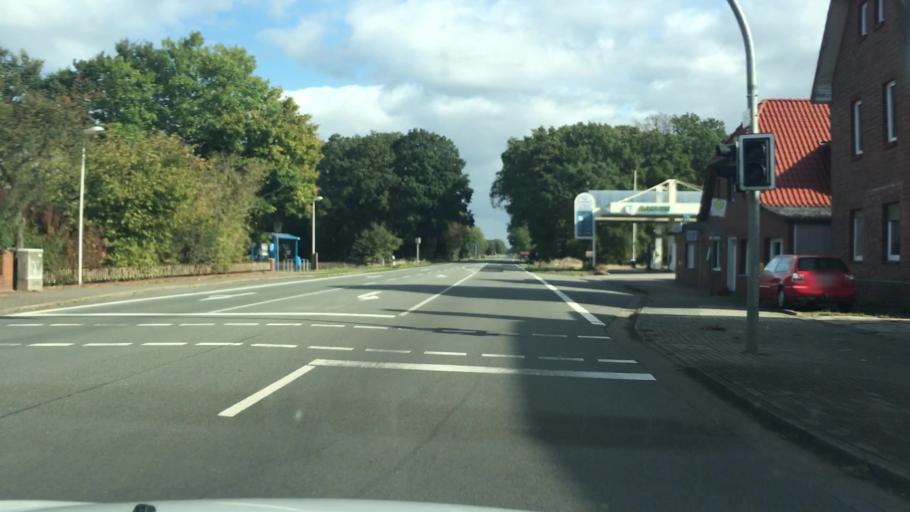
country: DE
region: Lower Saxony
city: Barver
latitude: 52.6090
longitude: 8.5870
